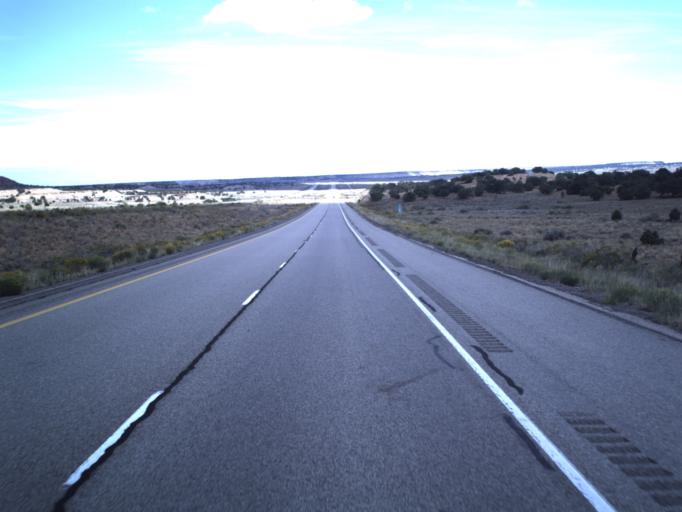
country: US
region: Utah
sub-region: Emery County
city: Castle Dale
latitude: 38.8677
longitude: -110.7034
